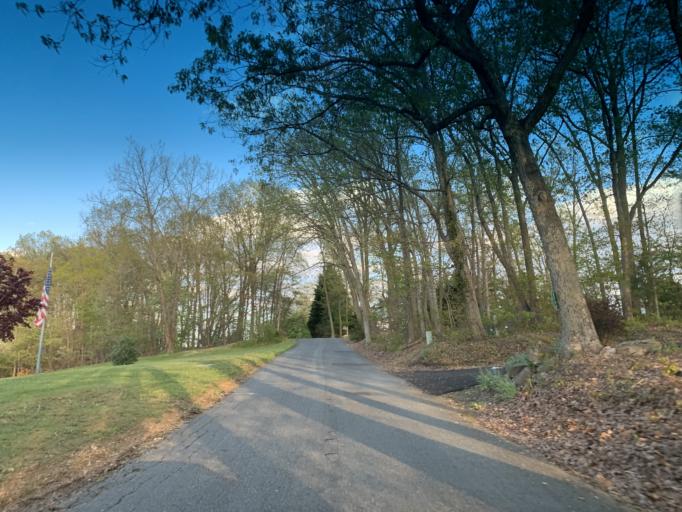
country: US
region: Maryland
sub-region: Harford County
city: Jarrettsville
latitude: 39.6242
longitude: -76.4273
